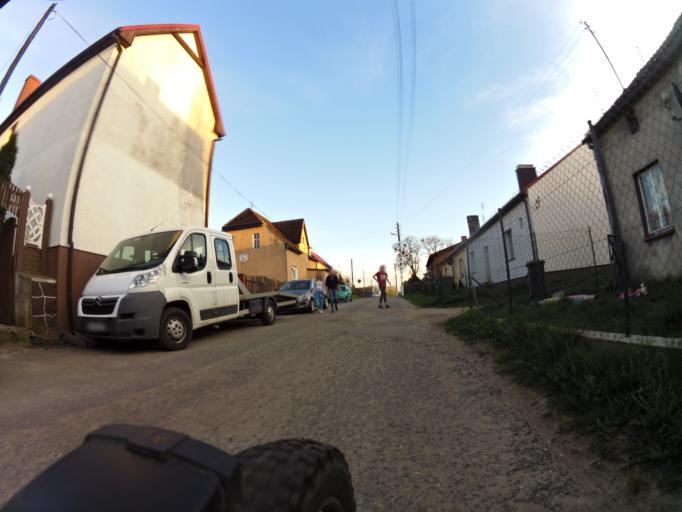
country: PL
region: West Pomeranian Voivodeship
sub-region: Powiat lobeski
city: Lobez
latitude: 53.7004
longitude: 15.6464
